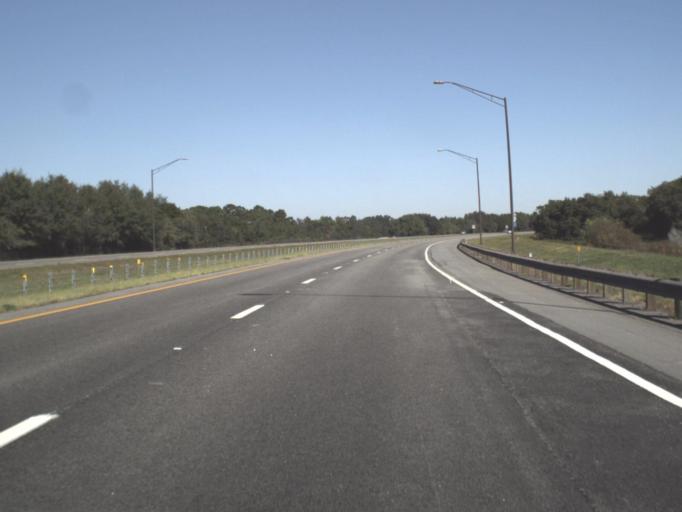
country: US
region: Florida
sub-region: Pasco County
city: Shady Hills
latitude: 28.3379
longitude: -82.5511
